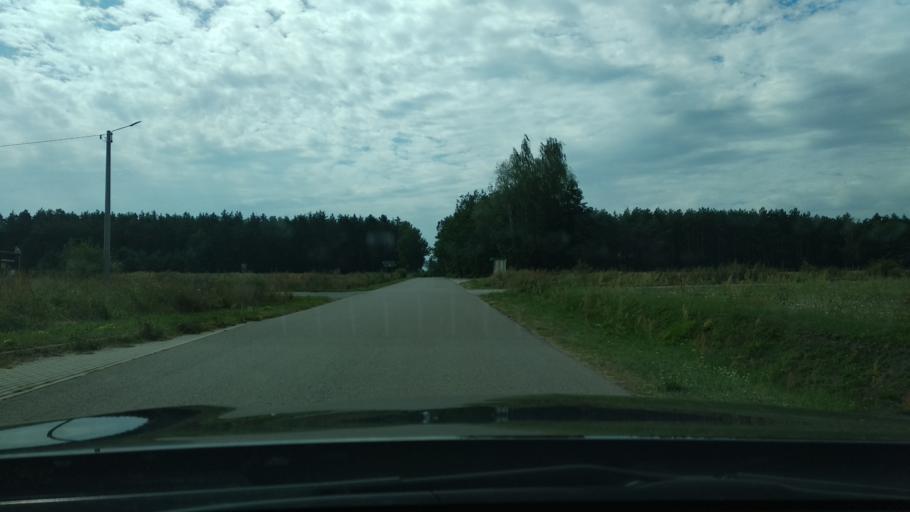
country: PL
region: Masovian Voivodeship
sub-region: Powiat pultuski
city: Zatory
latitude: 52.6434
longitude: 21.1842
